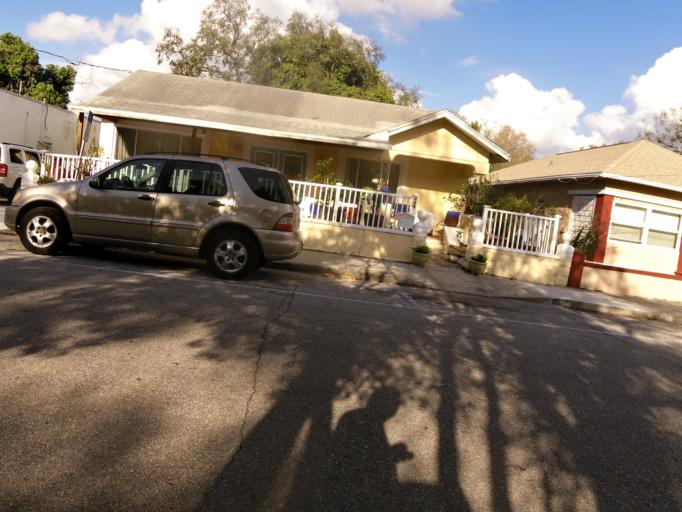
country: US
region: Florida
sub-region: Pinellas County
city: Tarpon Springs
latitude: 28.1535
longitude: -82.7596
